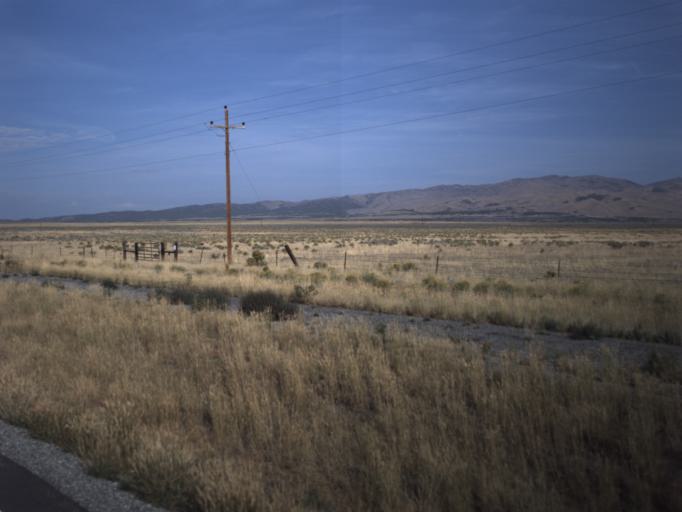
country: US
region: Idaho
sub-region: Oneida County
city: Malad City
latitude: 41.9658
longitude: -112.9993
